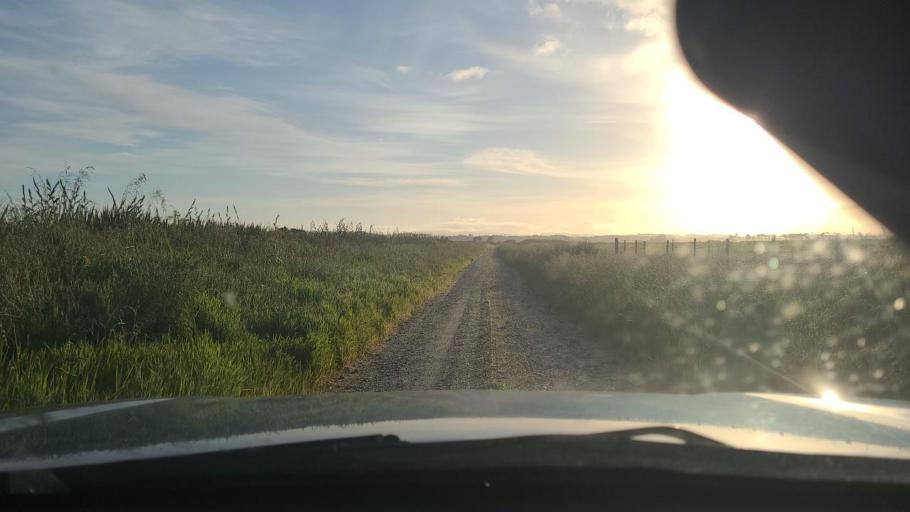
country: NZ
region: Southland
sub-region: Invercargill City
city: Invercargill
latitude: -46.4794
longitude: 168.7261
